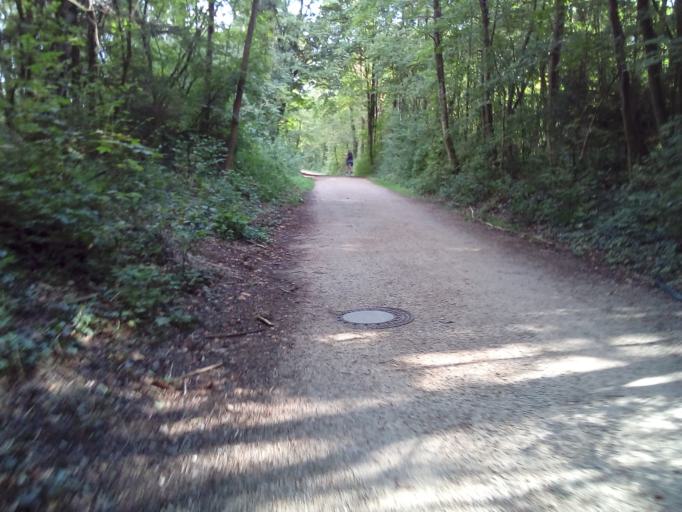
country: DE
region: Bavaria
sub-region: Upper Bavaria
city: Ismaning
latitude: 48.2338
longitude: 11.6710
